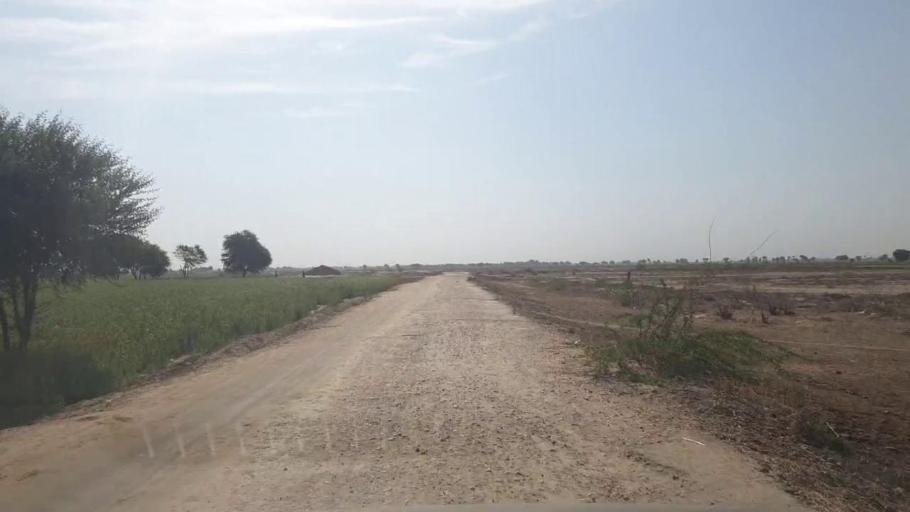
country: PK
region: Sindh
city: Umarkot
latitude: 25.2874
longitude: 69.6537
